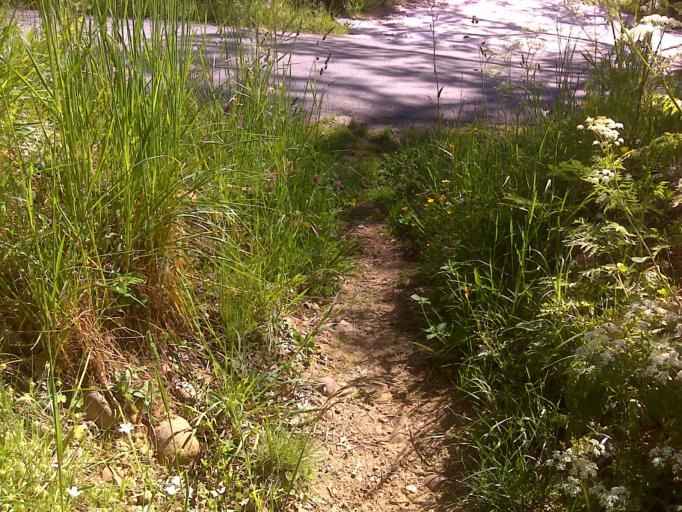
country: ES
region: Cantabria
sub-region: Provincia de Cantabria
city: San Pedro del Romeral
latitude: 43.0236
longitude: -3.7300
